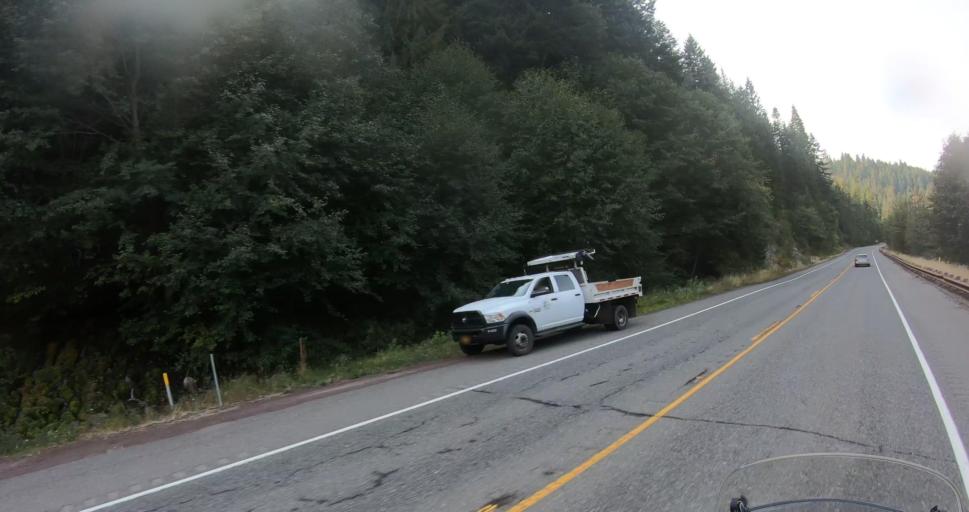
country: US
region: Oregon
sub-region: Hood River County
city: Odell
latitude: 45.4446
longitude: -121.5795
